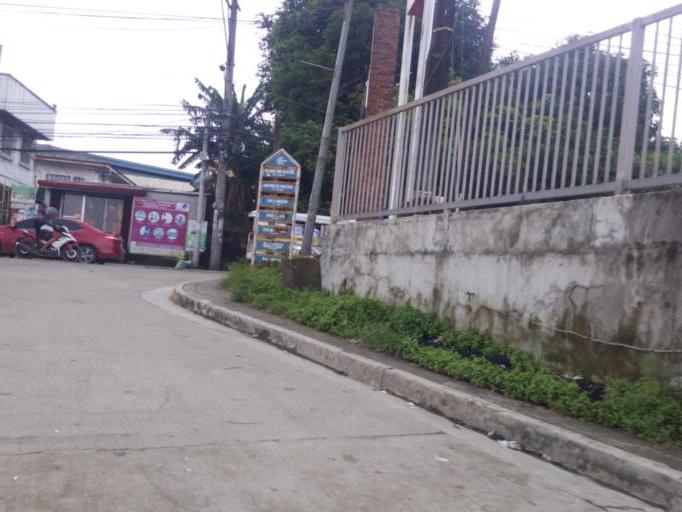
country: PH
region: Calabarzon
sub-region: Province of Rizal
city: Valenzuela
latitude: 14.7194
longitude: 121.0212
